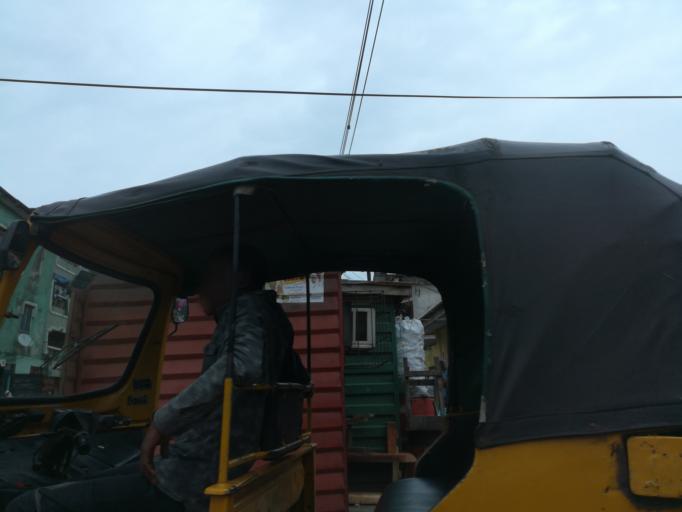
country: NG
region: Lagos
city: Ebute Metta
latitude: 6.4815
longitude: 3.3862
